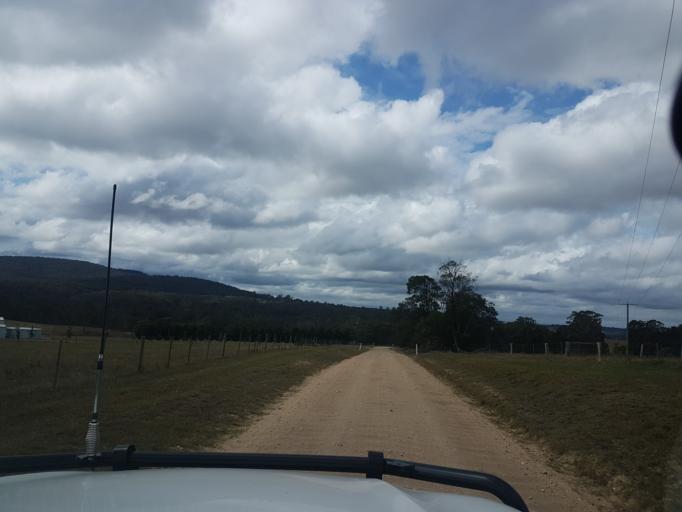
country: AU
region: Victoria
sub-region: East Gippsland
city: Bairnsdale
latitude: -37.7845
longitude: 147.5262
